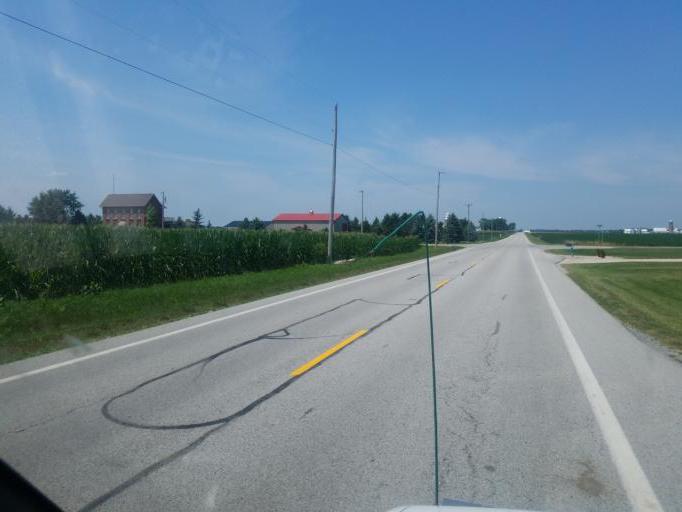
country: US
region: Ohio
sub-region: Auglaize County
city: New Bremen
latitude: 40.4508
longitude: -84.4340
